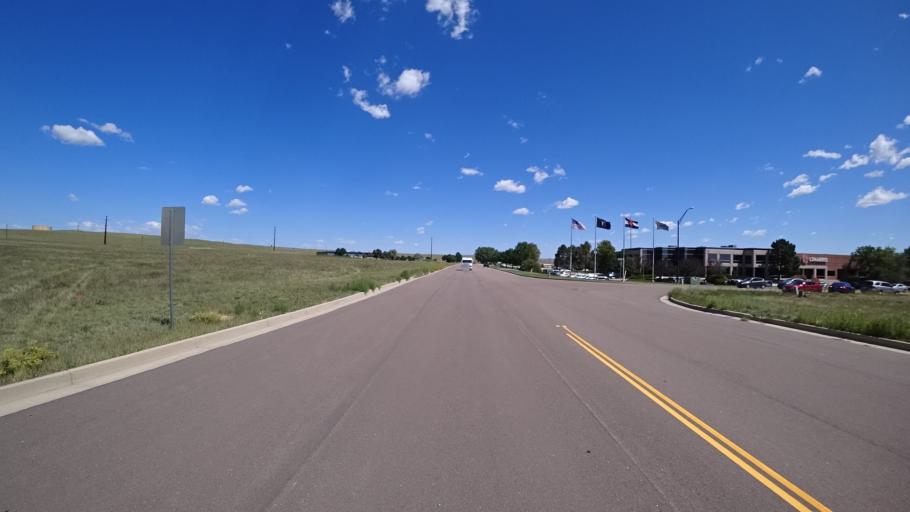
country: US
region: Colorado
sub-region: El Paso County
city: Security-Widefield
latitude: 38.7635
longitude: -104.6693
